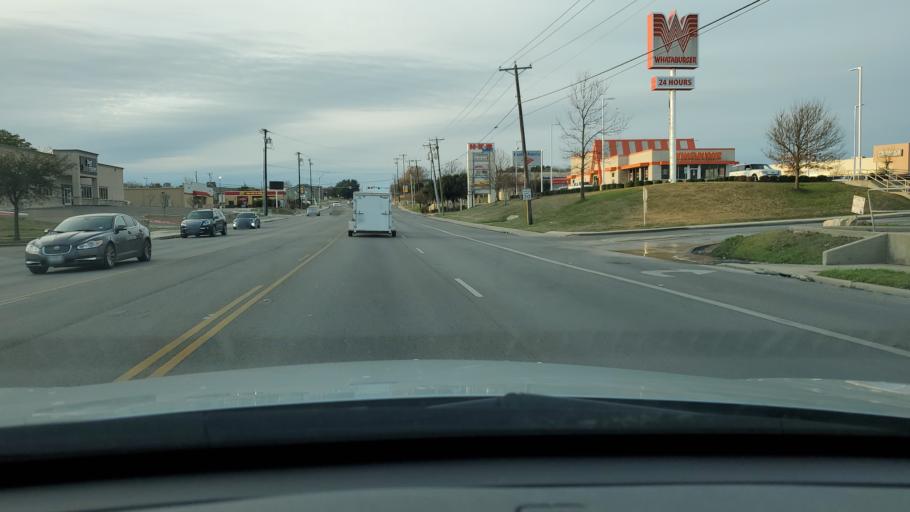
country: US
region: Texas
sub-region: Bell County
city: Killeen
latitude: 31.0920
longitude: -97.7334
